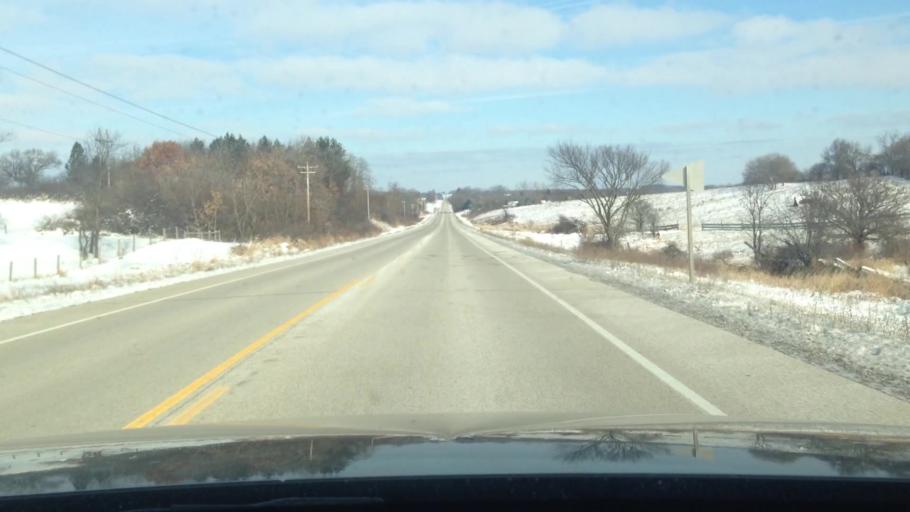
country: US
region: Wisconsin
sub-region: Walworth County
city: East Troy
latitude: 42.7006
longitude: -88.4049
